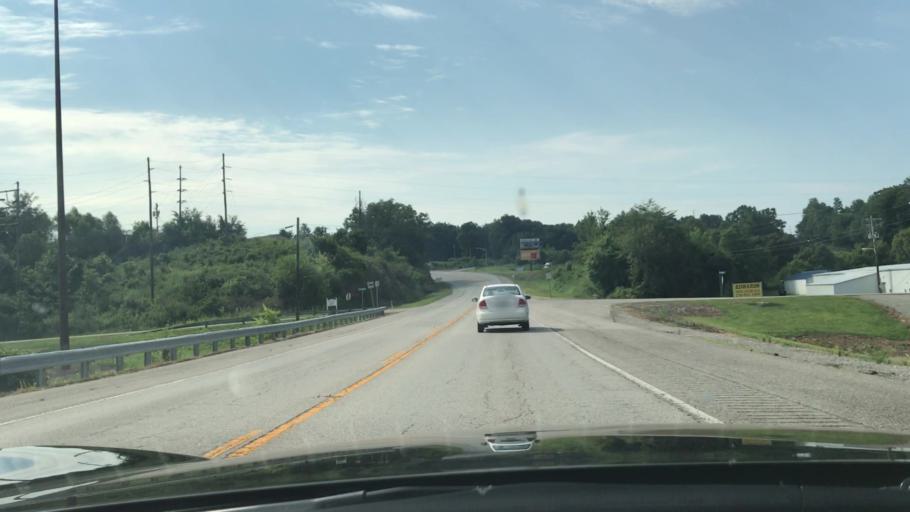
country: US
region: Kentucky
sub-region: Green County
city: Greensburg
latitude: 37.2769
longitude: -85.5113
